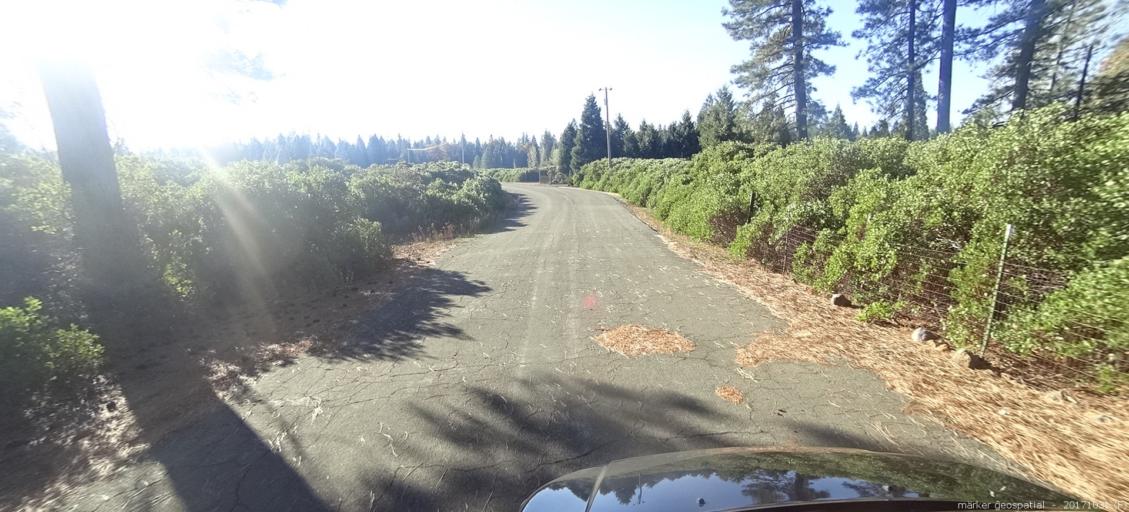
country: US
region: California
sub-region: Shasta County
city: Shingletown
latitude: 40.5245
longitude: -121.8399
